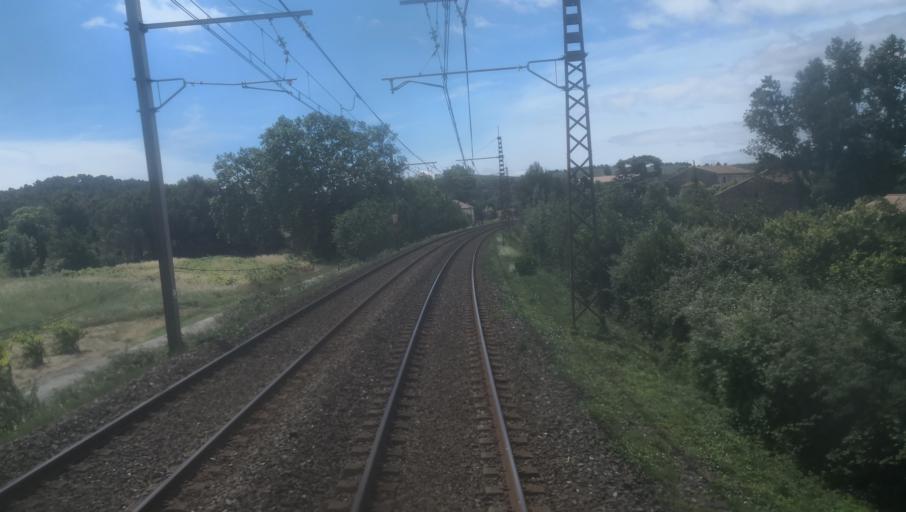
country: FR
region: Languedoc-Roussillon
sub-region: Departement de l'Aude
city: Nevian
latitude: 43.2109
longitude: 2.9068
